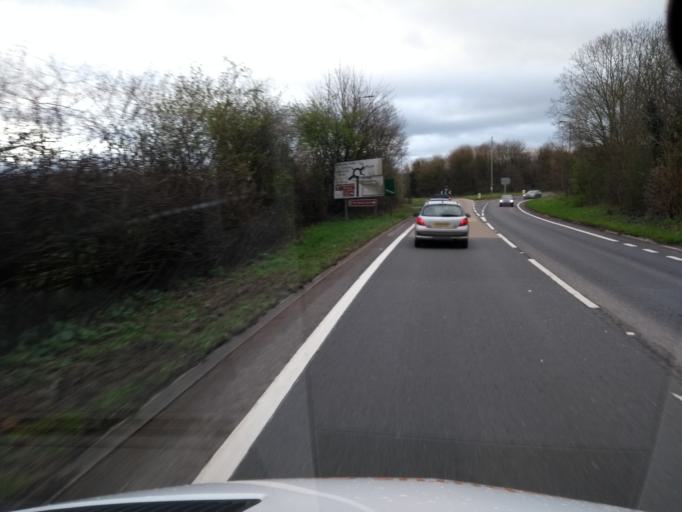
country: GB
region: England
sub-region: Somerset
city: Ilminster
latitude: 50.9348
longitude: -2.9378
